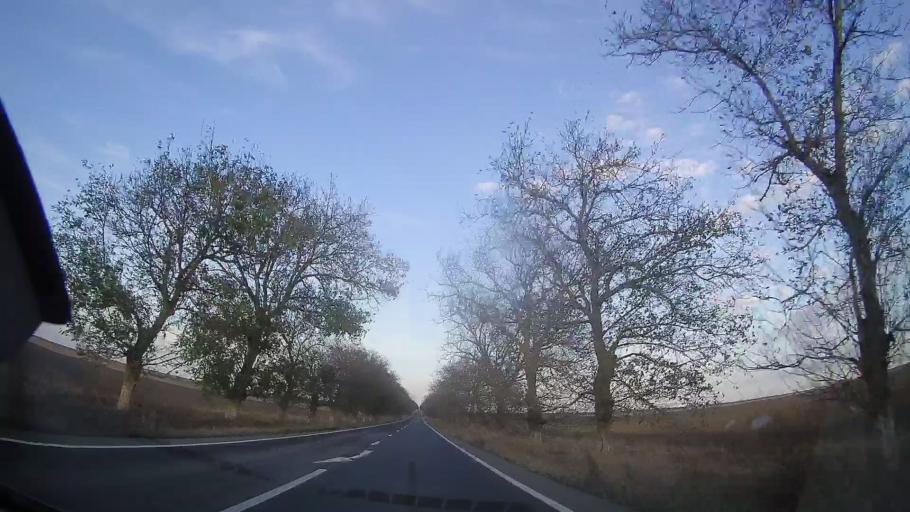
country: RO
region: Constanta
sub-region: Comuna Chirnogeni
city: Chirnogeni
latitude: 43.8569
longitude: 28.2520
